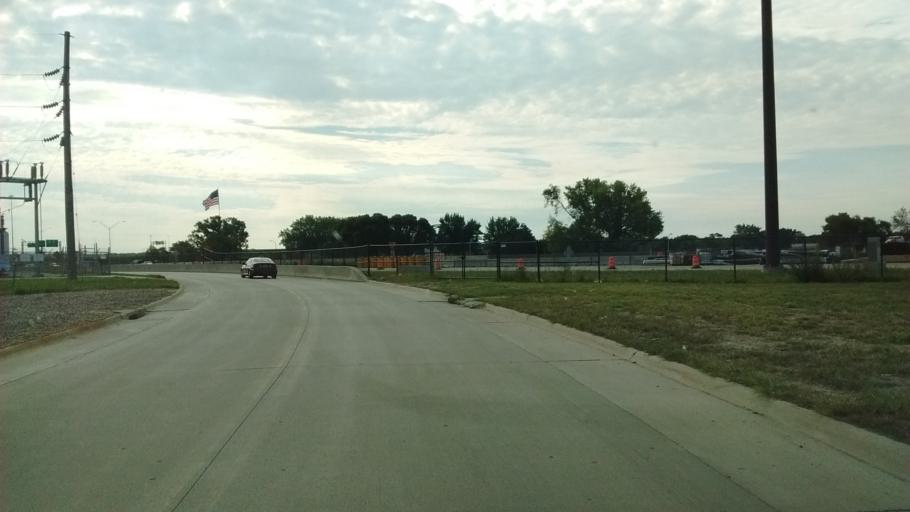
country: US
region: Nebraska
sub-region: Dakota County
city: South Sioux City
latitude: 42.4929
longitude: -96.4208
